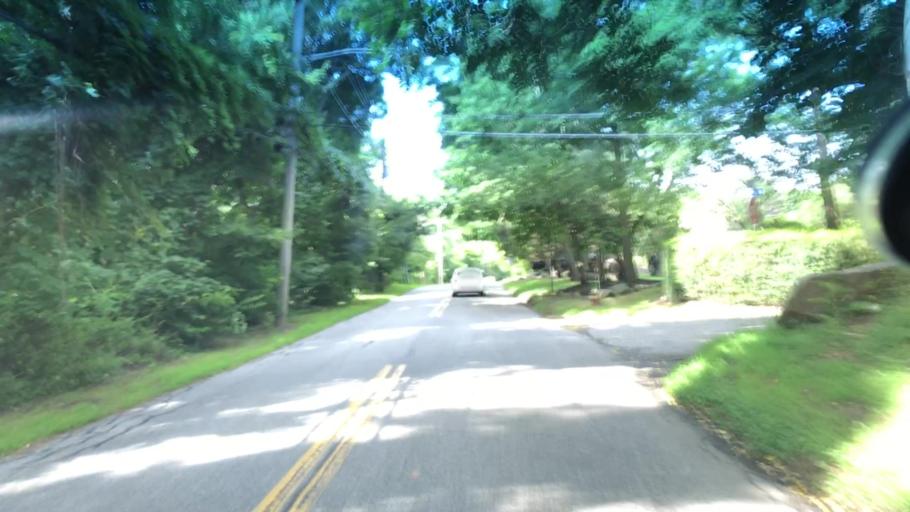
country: US
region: New York
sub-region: Suffolk County
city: Wading River
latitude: 40.9620
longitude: -72.8284
